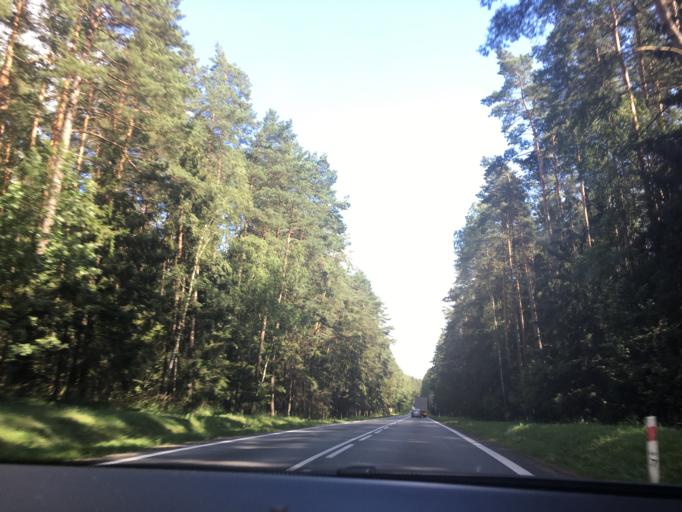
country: PL
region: Podlasie
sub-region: Powiat bialostocki
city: Wasilkow
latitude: 53.2585
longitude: 23.1396
